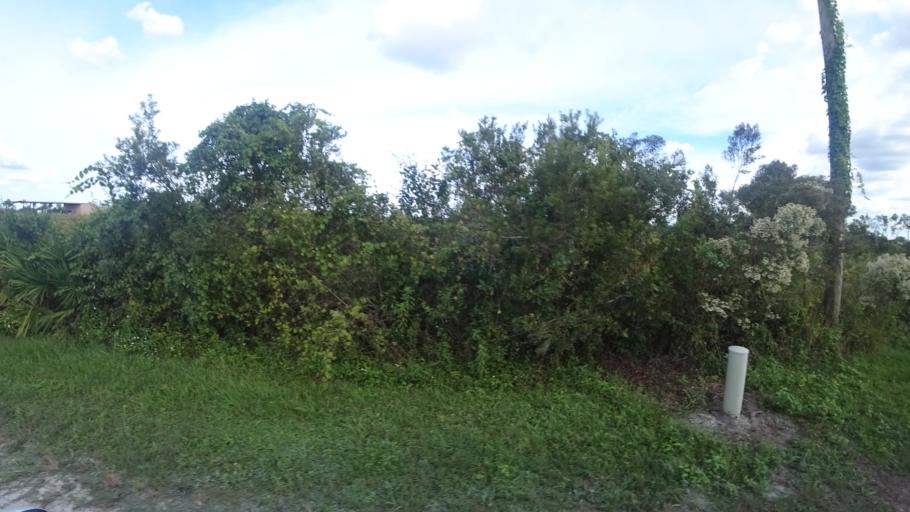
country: US
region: Florida
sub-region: DeSoto County
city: Arcadia
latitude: 27.2949
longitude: -82.1053
